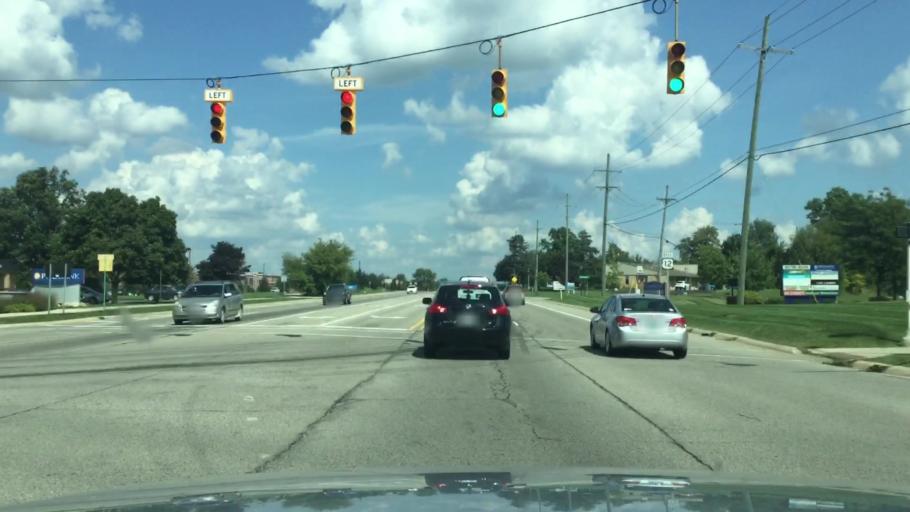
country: US
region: Michigan
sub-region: Washtenaw County
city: Saline
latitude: 42.1849
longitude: -83.7389
